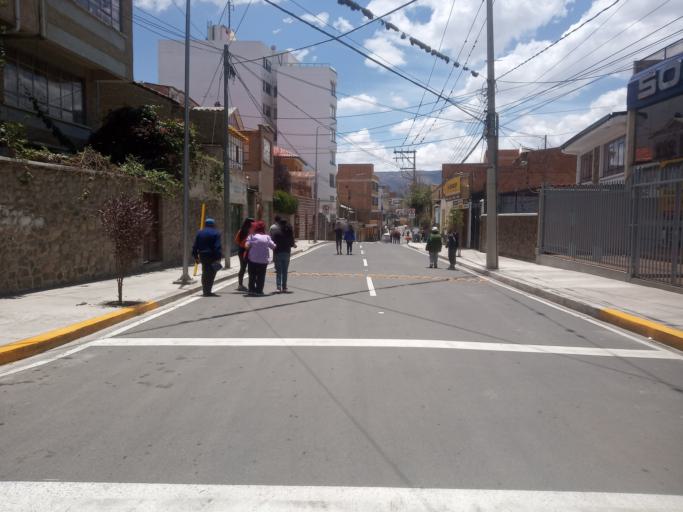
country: BO
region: La Paz
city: La Paz
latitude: -16.5125
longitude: -68.1336
